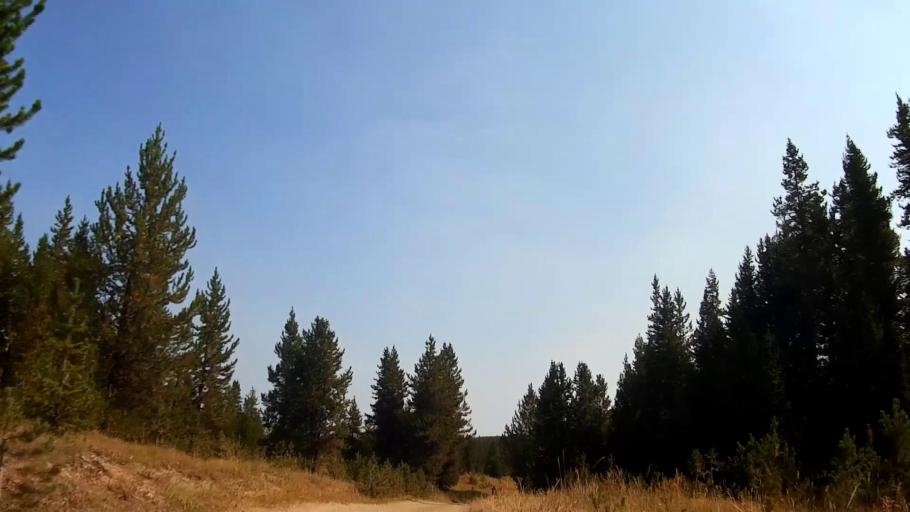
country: US
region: Montana
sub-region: Gallatin County
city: West Yellowstone
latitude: 44.5750
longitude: -111.1851
